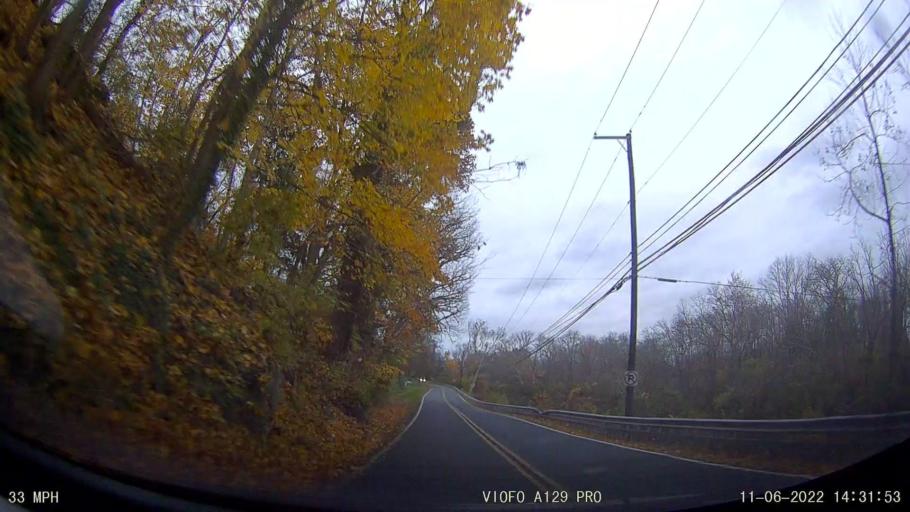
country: US
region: Pennsylvania
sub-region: Berks County
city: Spring Ridge
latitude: 40.3624
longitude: -75.9721
